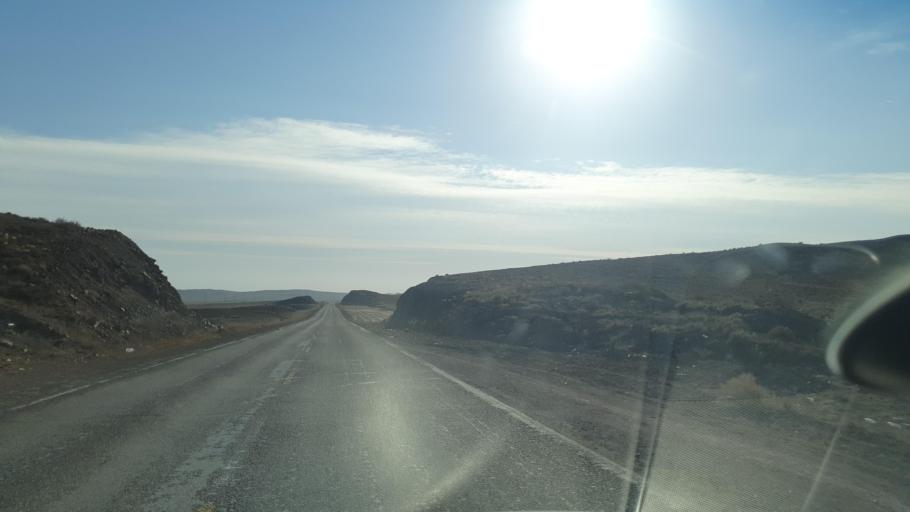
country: KZ
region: Zhambyl
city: Mynaral
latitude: 45.6995
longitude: 73.3993
